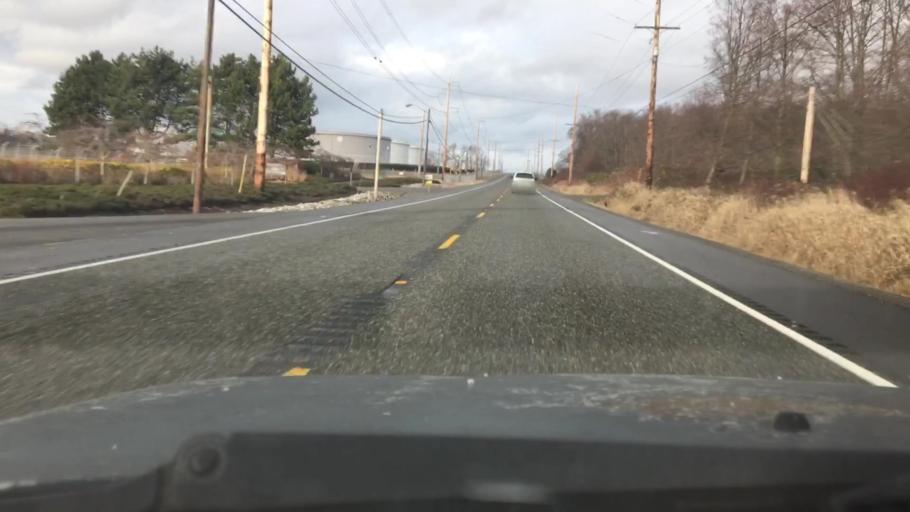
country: US
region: Washington
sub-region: Whatcom County
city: Ferndale
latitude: 48.8280
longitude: -122.6825
